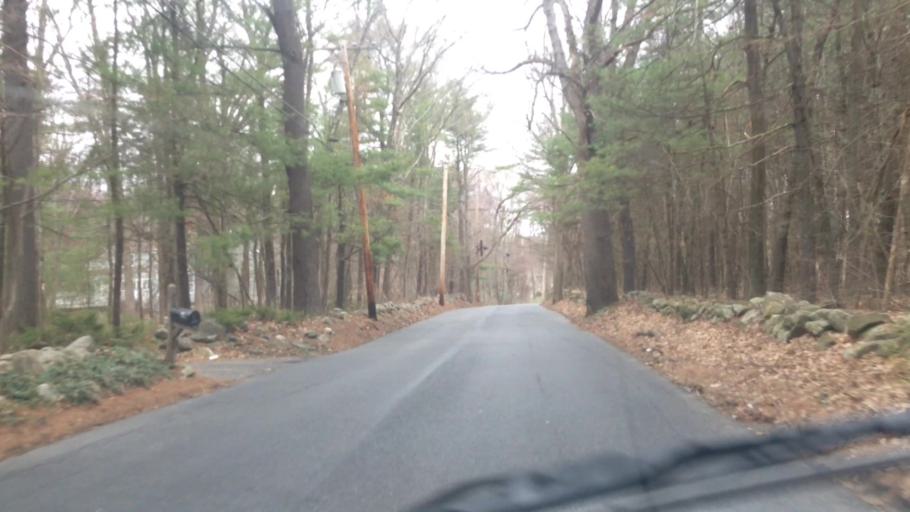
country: US
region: Massachusetts
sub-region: Middlesex County
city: Acton
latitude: 42.4917
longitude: -71.4101
